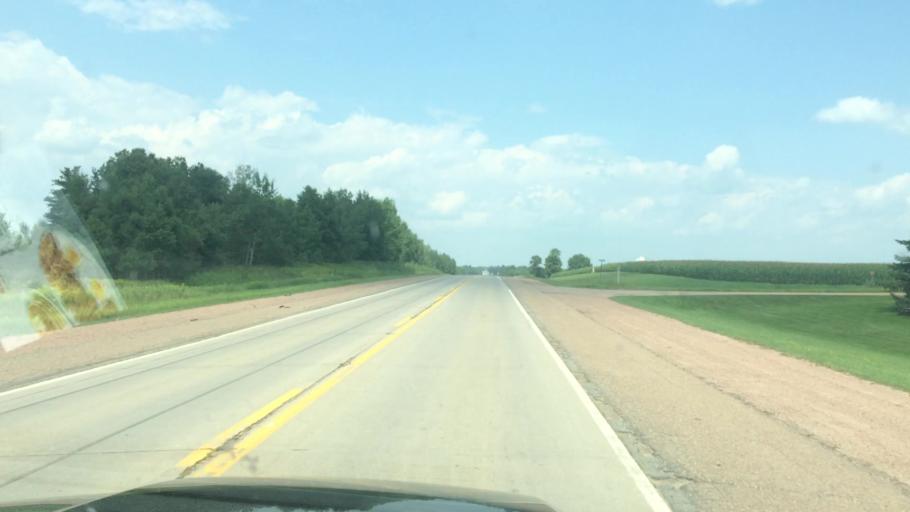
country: US
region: Wisconsin
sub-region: Clark County
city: Colby
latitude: 44.8801
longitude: -90.3156
